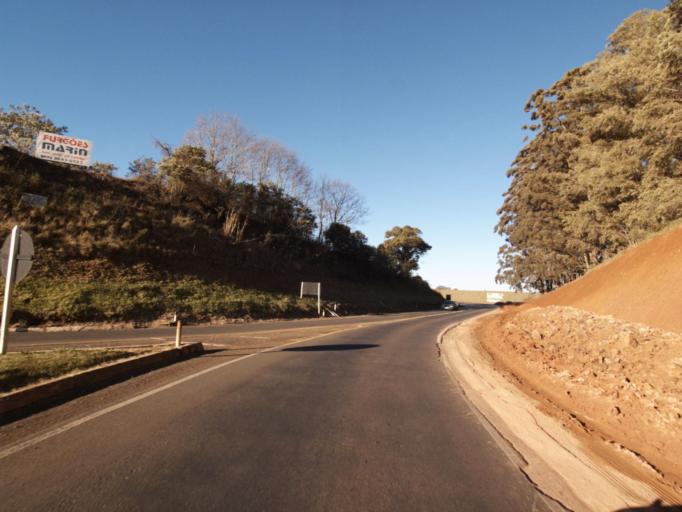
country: AR
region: Misiones
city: Bernardo de Irigoyen
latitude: -26.2873
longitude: -53.5554
